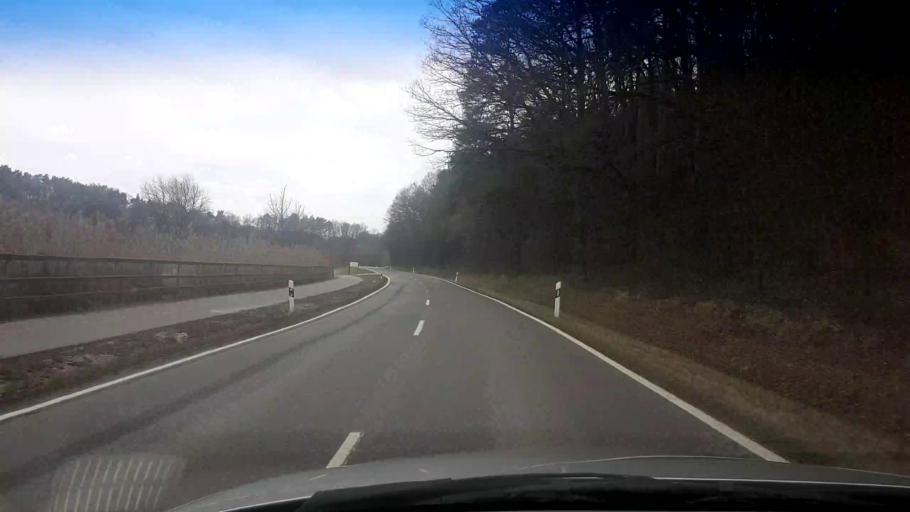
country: DE
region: Bavaria
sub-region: Upper Franconia
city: Priesendorf
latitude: 49.9141
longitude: 10.6904
